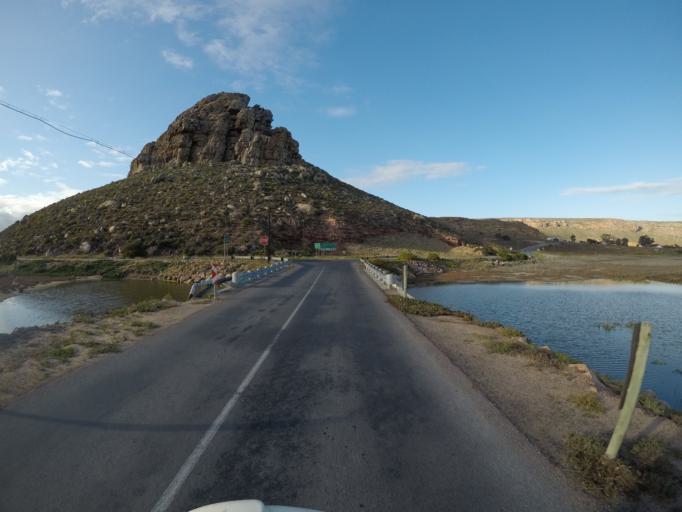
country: ZA
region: Western Cape
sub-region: West Coast District Municipality
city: Clanwilliam
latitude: -32.3151
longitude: 18.3552
